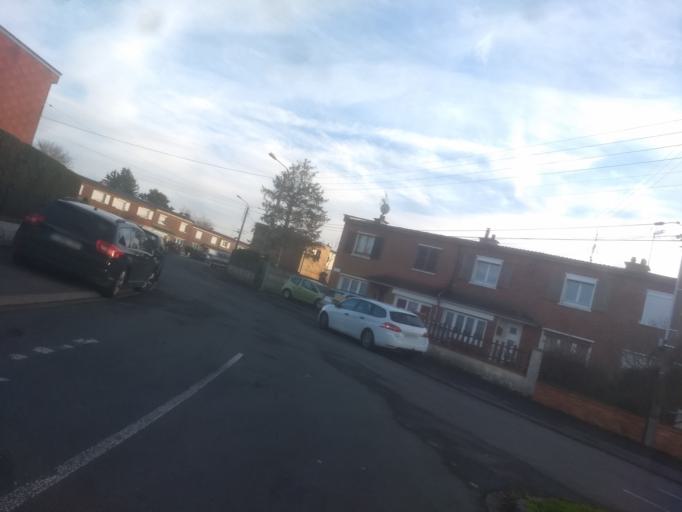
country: FR
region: Nord-Pas-de-Calais
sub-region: Departement du Pas-de-Calais
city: Beaurains
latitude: 50.2718
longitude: 2.7916
